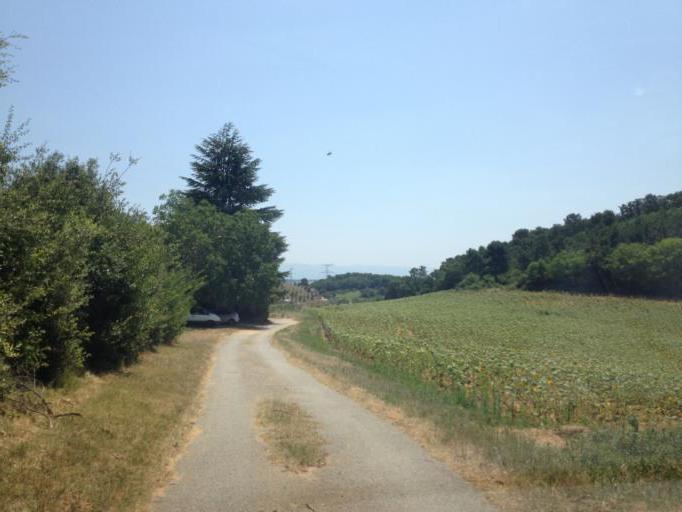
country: FR
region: Rhone-Alpes
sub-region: Departement de la Drome
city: Clerieux
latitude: 45.1340
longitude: 4.9316
